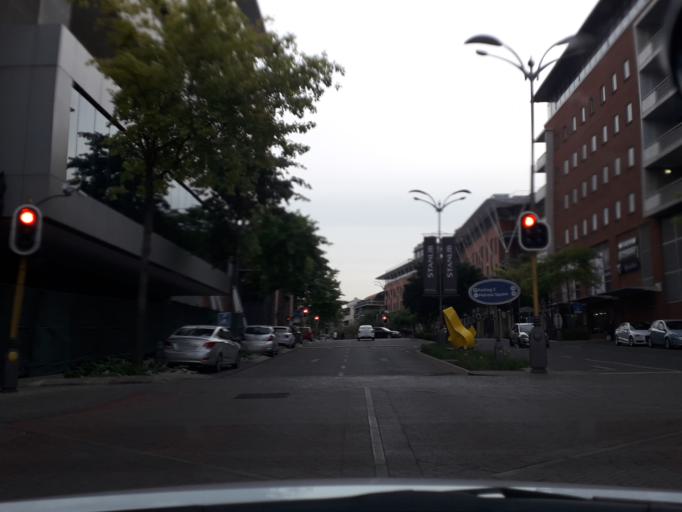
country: ZA
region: Gauteng
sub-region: City of Johannesburg Metropolitan Municipality
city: Johannesburg
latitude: -26.1321
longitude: 28.0694
